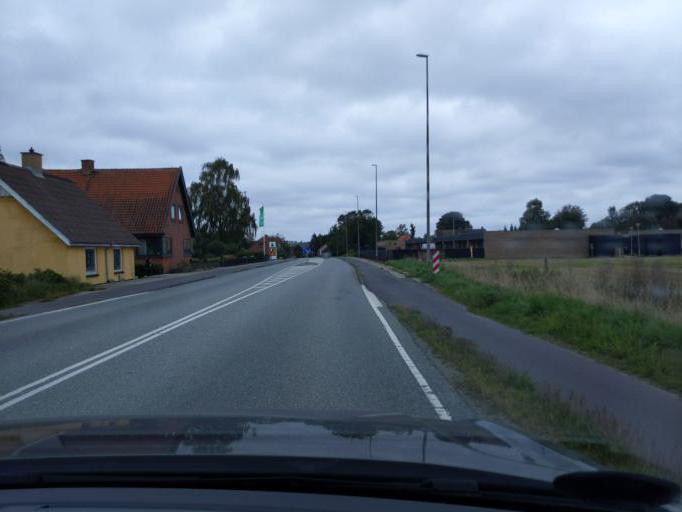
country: DK
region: Central Jutland
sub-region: Randers Kommune
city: Spentrup
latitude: 56.5112
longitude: 9.9518
